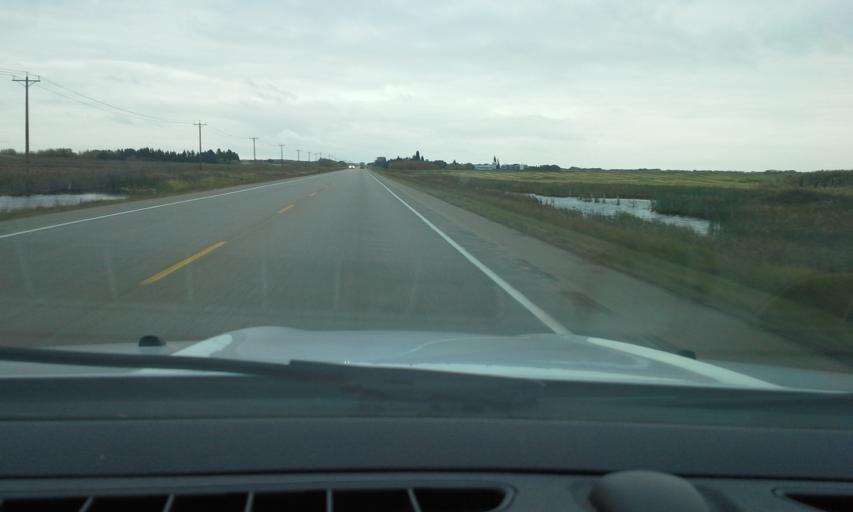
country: CA
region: Saskatchewan
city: Lloydminster
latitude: 53.2780
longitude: -109.8677
